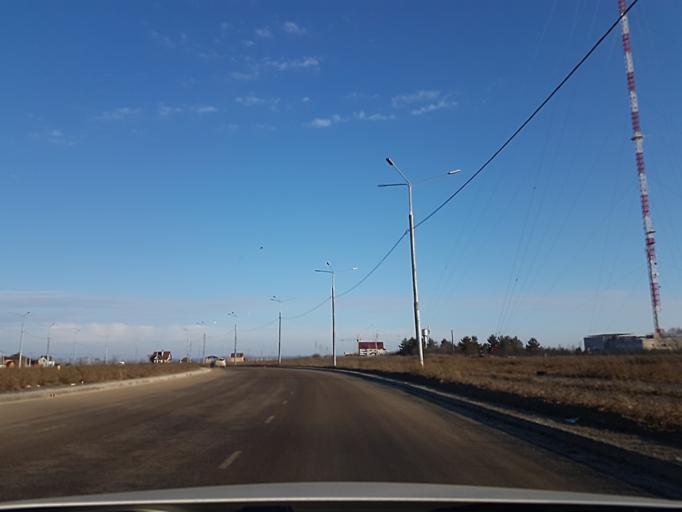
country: RU
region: Tambov
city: Tambov
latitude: 52.7812
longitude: 41.4090
